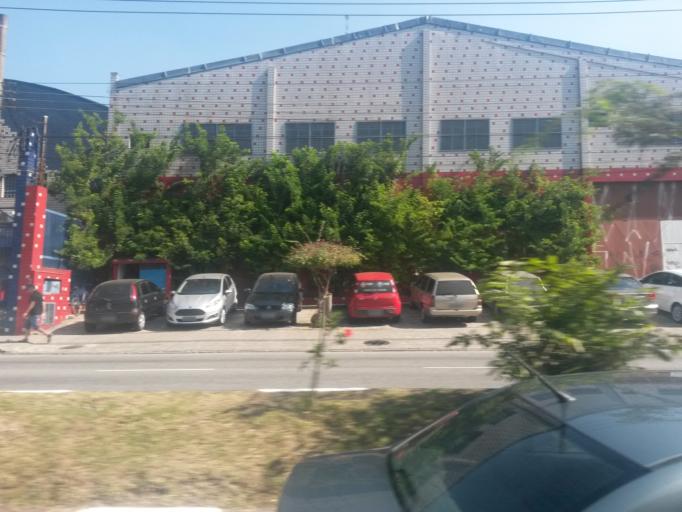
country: BR
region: Sao Paulo
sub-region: Sao Bernardo Do Campo
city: Sao Bernardo do Campo
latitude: -23.7320
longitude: -46.5445
